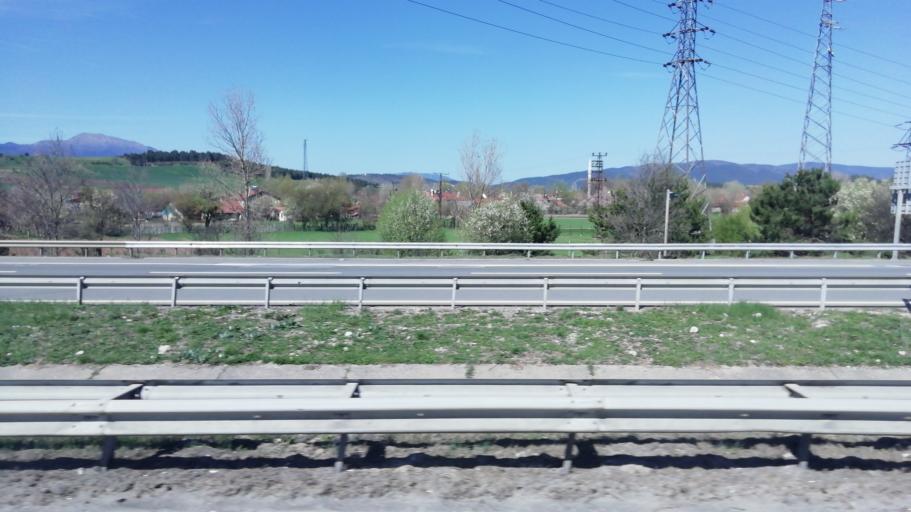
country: TR
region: Bolu
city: Bolu
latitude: 40.7637
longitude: 31.7564
